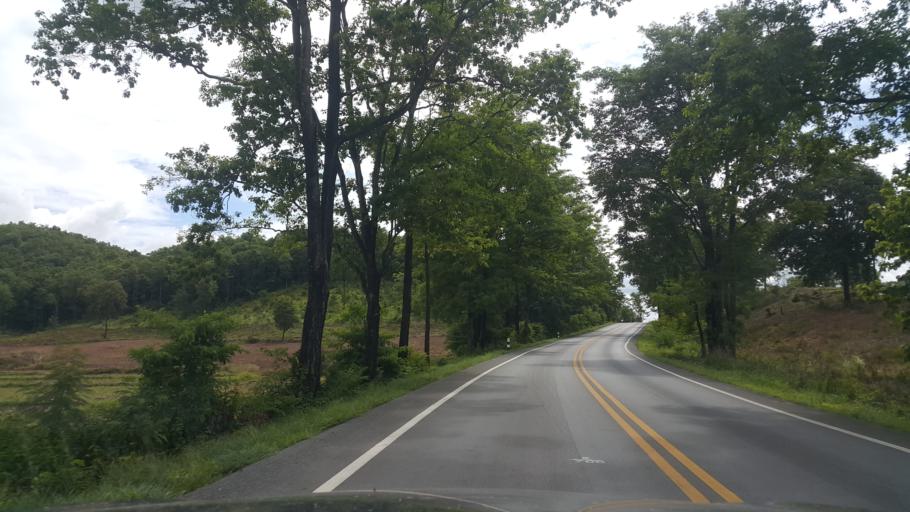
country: TH
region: Uttaradit
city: Thong Saen Khan
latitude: 17.3708
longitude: 100.2556
